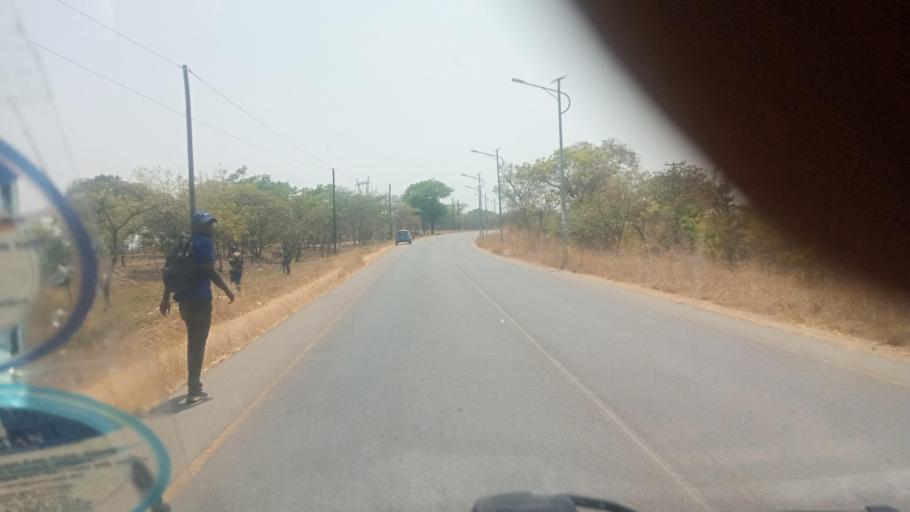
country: ZM
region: Lusaka
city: Lusaka
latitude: -15.4698
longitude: 28.4272
